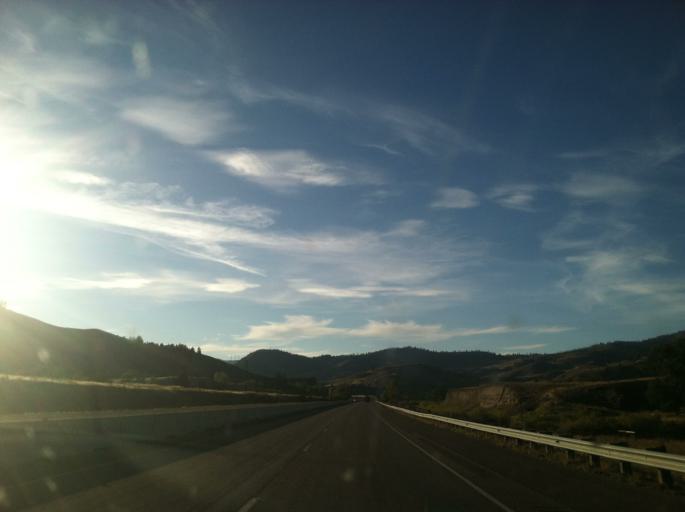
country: US
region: Montana
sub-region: Granite County
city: Philipsburg
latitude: 46.7075
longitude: -113.2571
